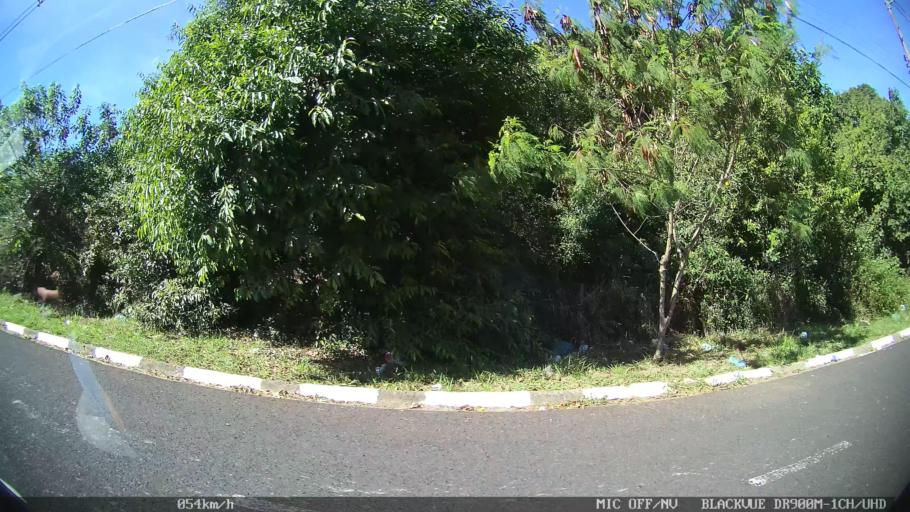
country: BR
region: Sao Paulo
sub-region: Franca
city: Franca
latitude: -20.5303
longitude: -47.3733
